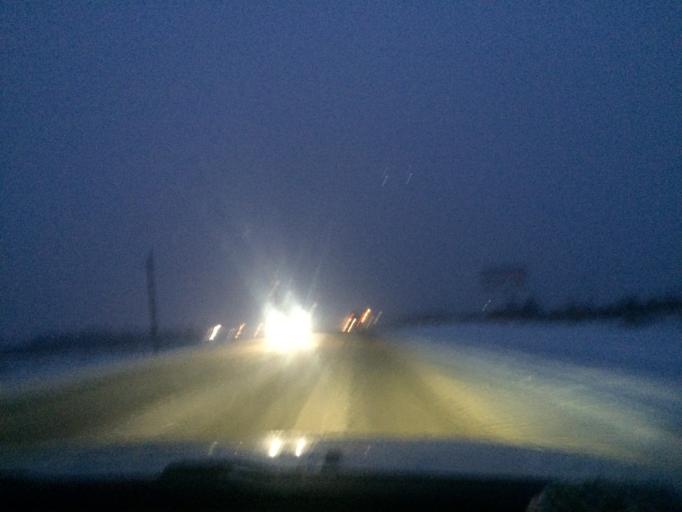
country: RU
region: Tula
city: Kosaya Gora
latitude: 54.1601
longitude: 37.4772
